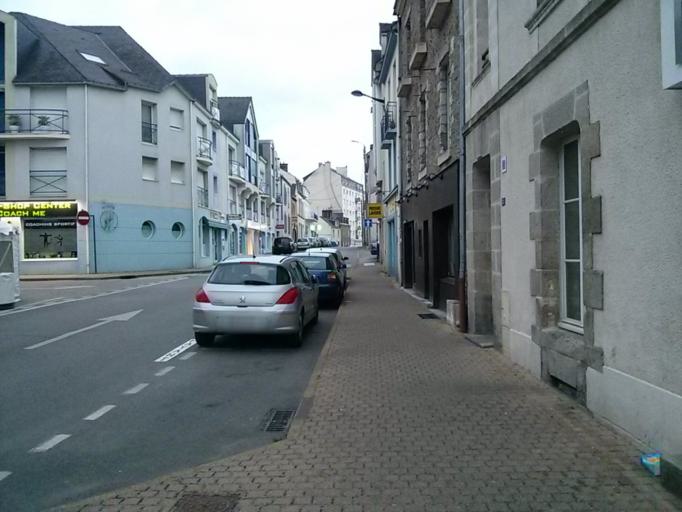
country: FR
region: Brittany
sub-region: Departement du Morbihan
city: Vannes
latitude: 47.6583
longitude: -2.7496
